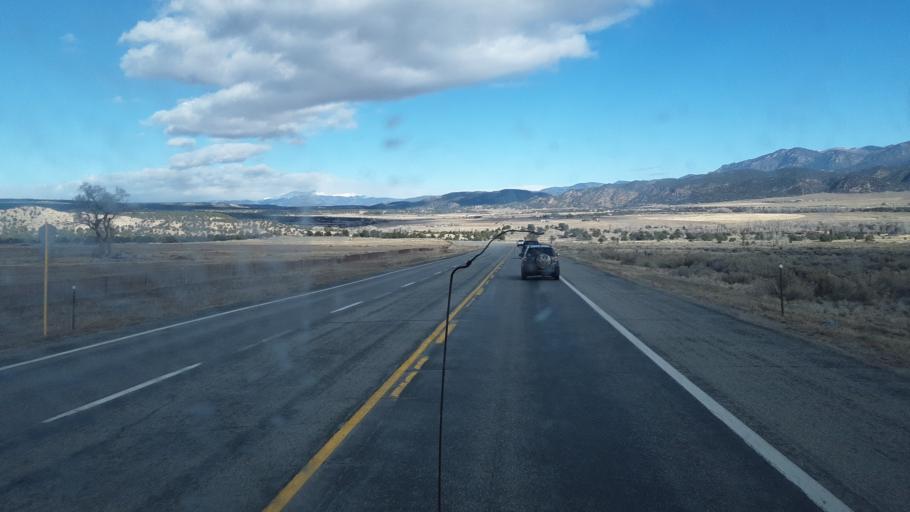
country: US
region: Colorado
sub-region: Chaffee County
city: Salida
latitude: 38.5630
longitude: -106.0807
